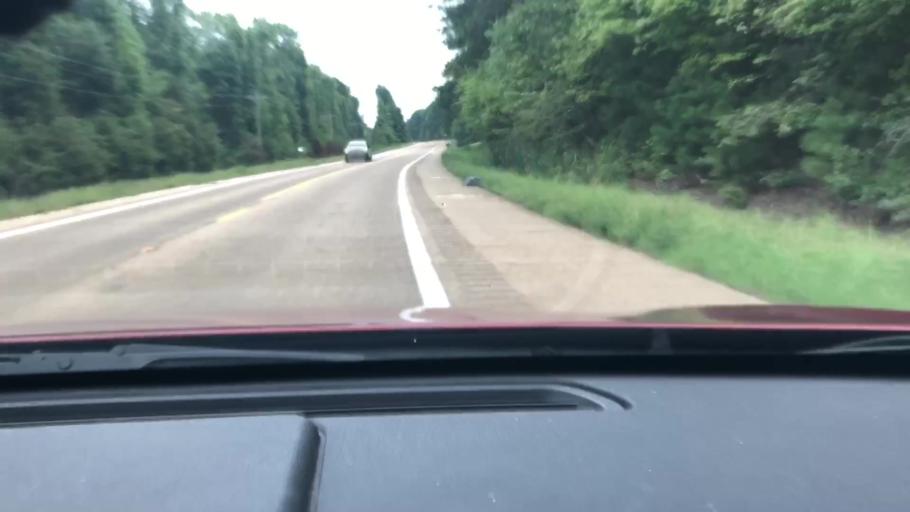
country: US
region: Arkansas
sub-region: Miller County
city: Texarkana
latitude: 33.4192
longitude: -93.8365
